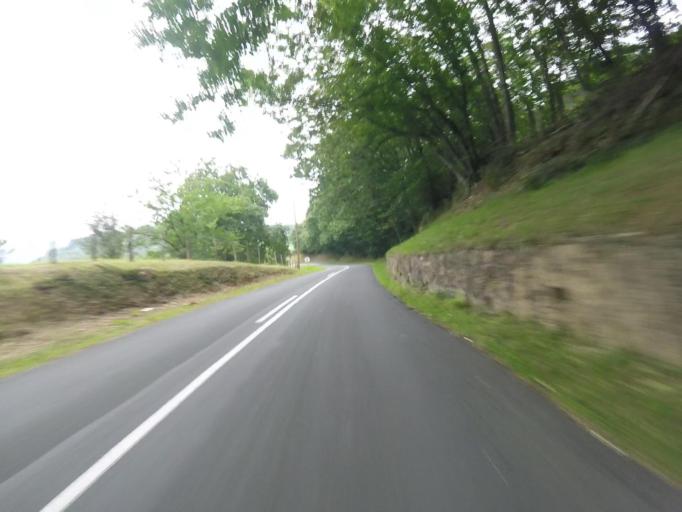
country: ES
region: Basque Country
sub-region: Provincia de Guipuzcoa
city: Lezo
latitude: 43.3124
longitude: -1.8528
